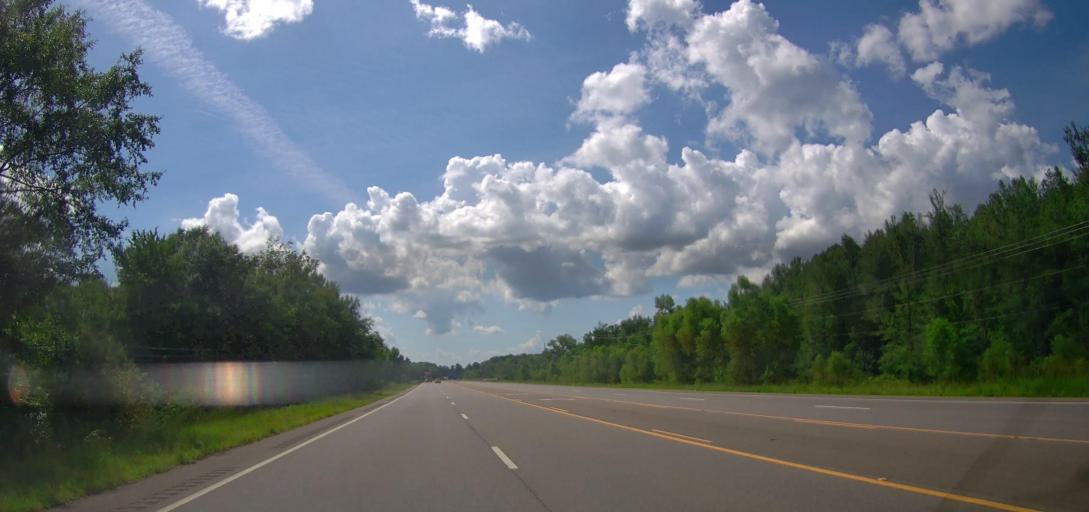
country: US
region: Alabama
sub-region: Pickens County
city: Reform
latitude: 33.3728
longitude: -88.0010
